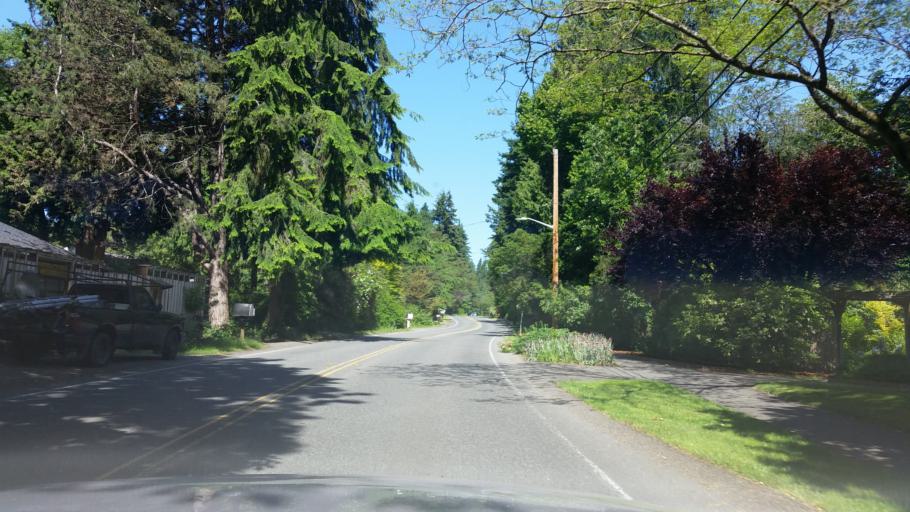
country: US
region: Washington
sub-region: King County
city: Lake Forest Park
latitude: 47.7532
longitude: -122.2829
